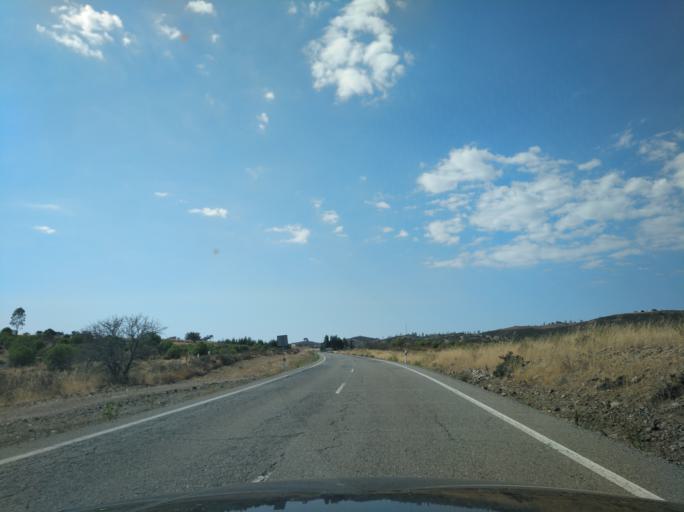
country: ES
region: Andalusia
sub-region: Provincia de Huelva
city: Santa Barbara de Casa
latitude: 37.7839
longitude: -7.1636
